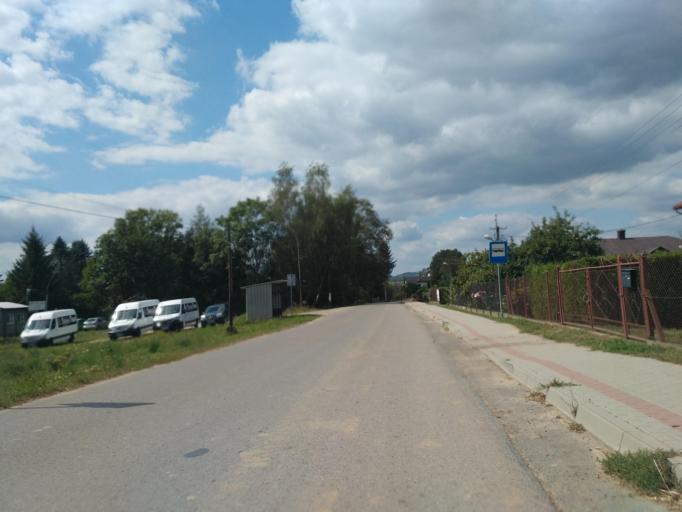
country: PL
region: Subcarpathian Voivodeship
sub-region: Powiat rzeszowski
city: Dynow
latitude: 49.8128
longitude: 22.2583
